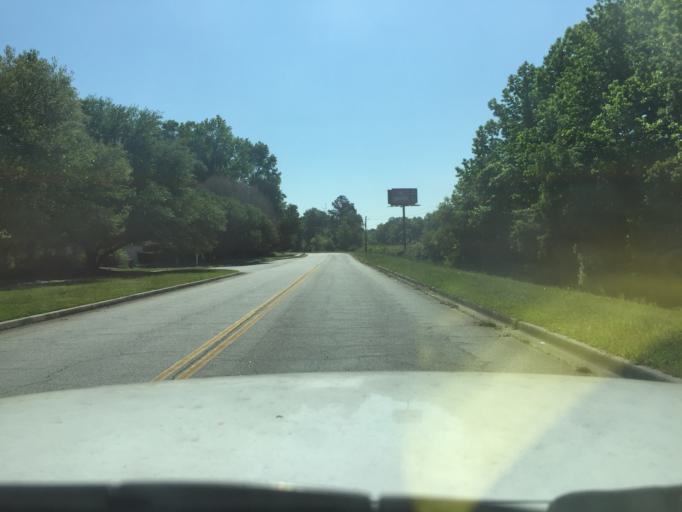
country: US
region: Georgia
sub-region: Chatham County
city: Georgetown
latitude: 32.0025
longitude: -81.2631
